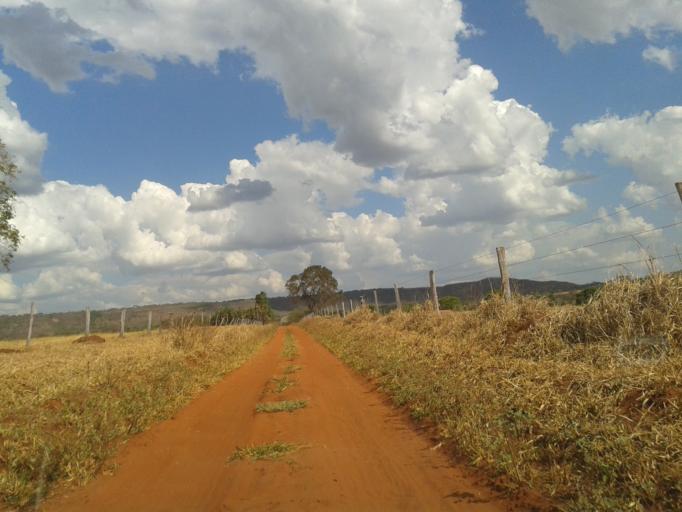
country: BR
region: Minas Gerais
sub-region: Santa Vitoria
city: Santa Vitoria
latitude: -19.2062
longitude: -49.9688
